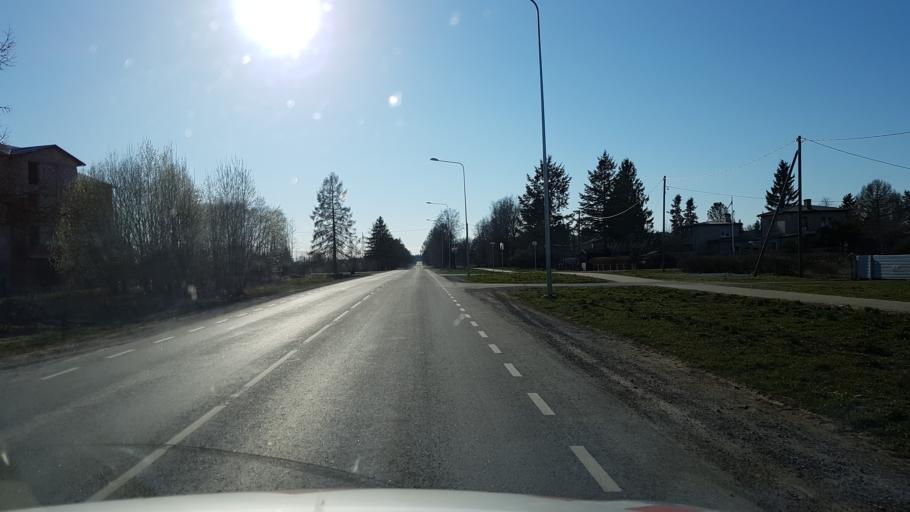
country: EE
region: Ida-Virumaa
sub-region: Johvi vald
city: Johvi
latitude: 59.3518
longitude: 27.4061
